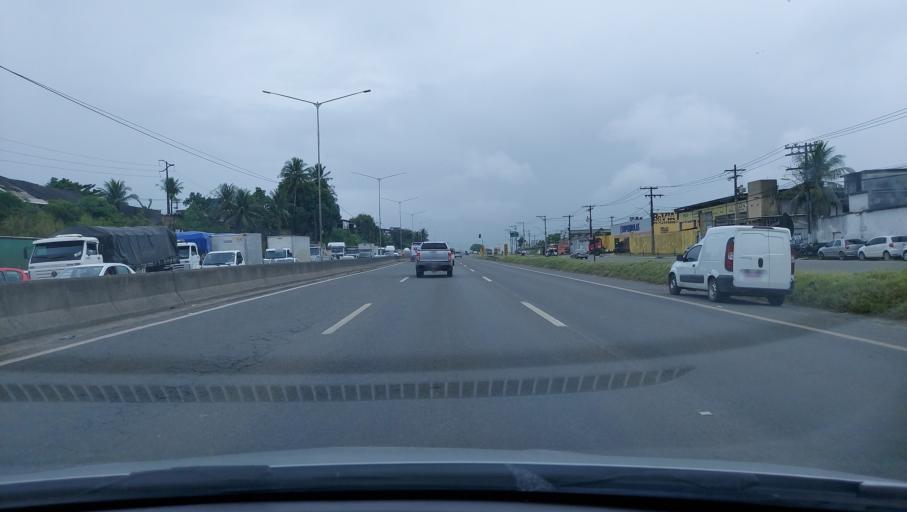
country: BR
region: Bahia
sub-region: Salvador
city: Salvador
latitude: -12.8946
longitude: -38.4477
